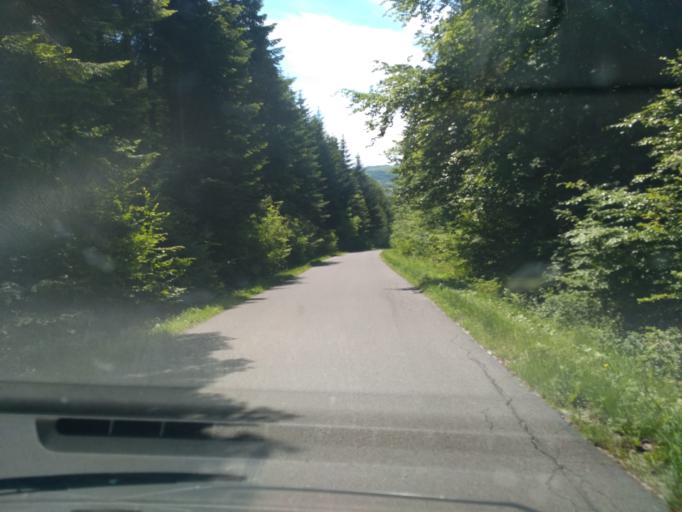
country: PL
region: Subcarpathian Voivodeship
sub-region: Powiat strzyzowski
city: Polomia
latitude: 49.9101
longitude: 21.9031
